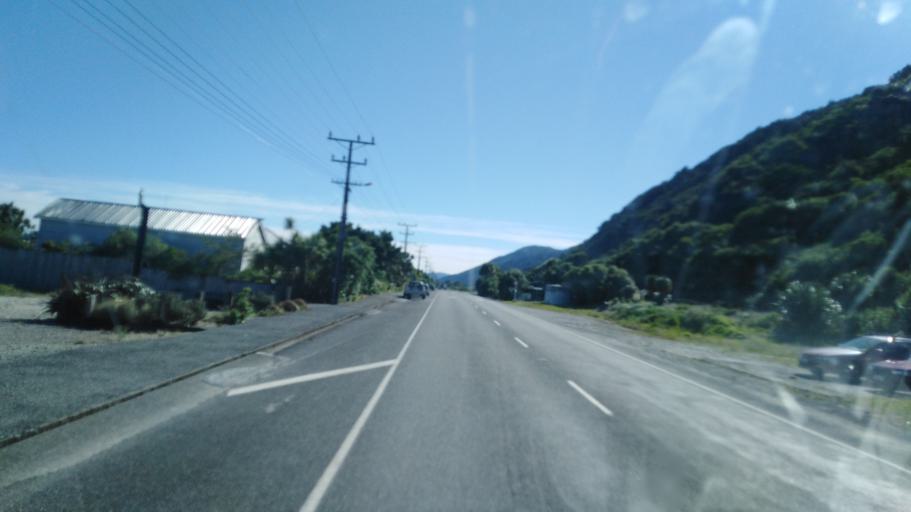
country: NZ
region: West Coast
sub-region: Buller District
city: Westport
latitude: -41.6245
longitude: 171.8587
